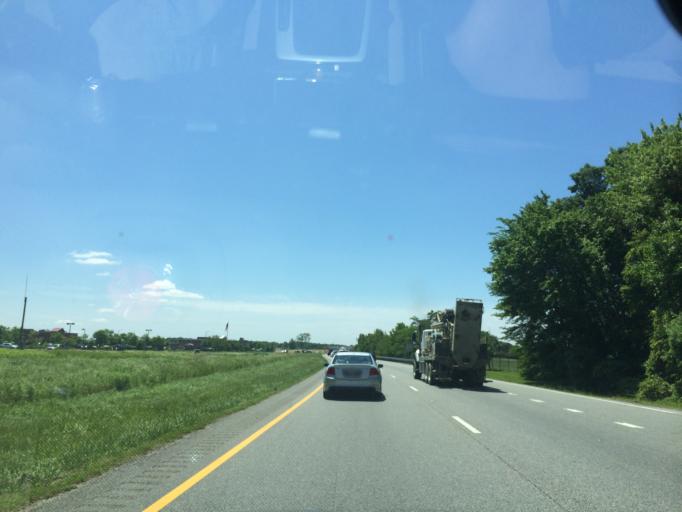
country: US
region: Maryland
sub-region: Talbot County
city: Easton
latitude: 38.7978
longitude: -76.0607
